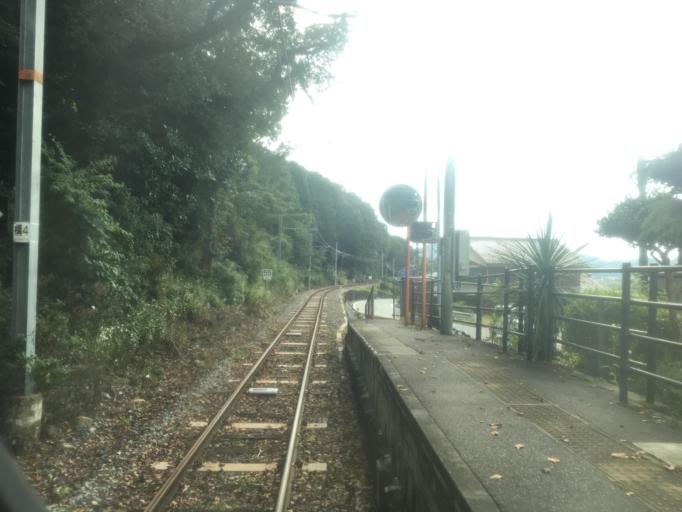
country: JP
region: Hyogo
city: Nishiwaki
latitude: 35.0635
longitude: 135.0097
